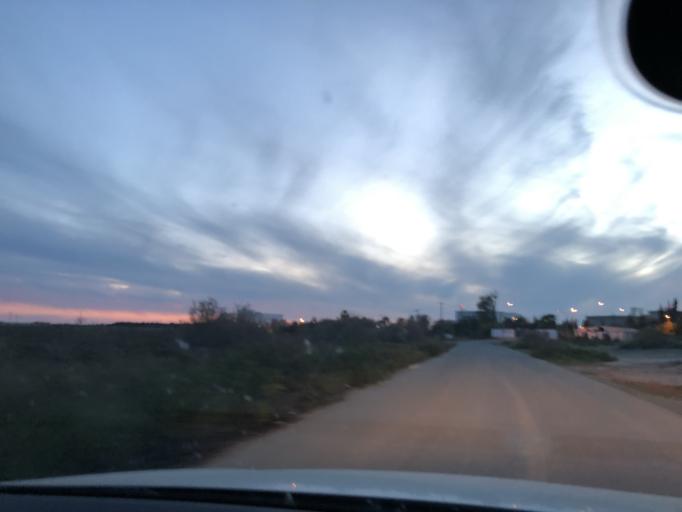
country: CY
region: Larnaka
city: Meneou
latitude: 34.8689
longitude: 33.6338
